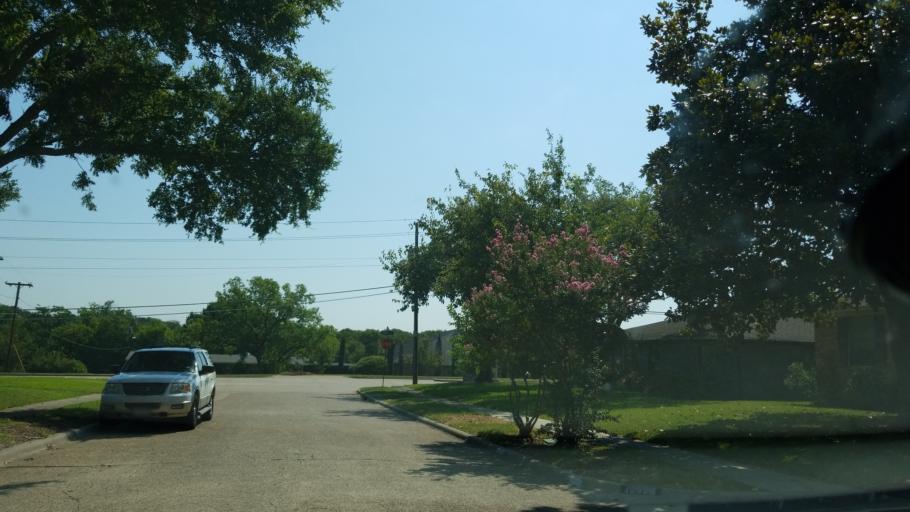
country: US
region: Texas
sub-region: Dallas County
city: Garland
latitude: 32.8750
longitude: -96.7007
